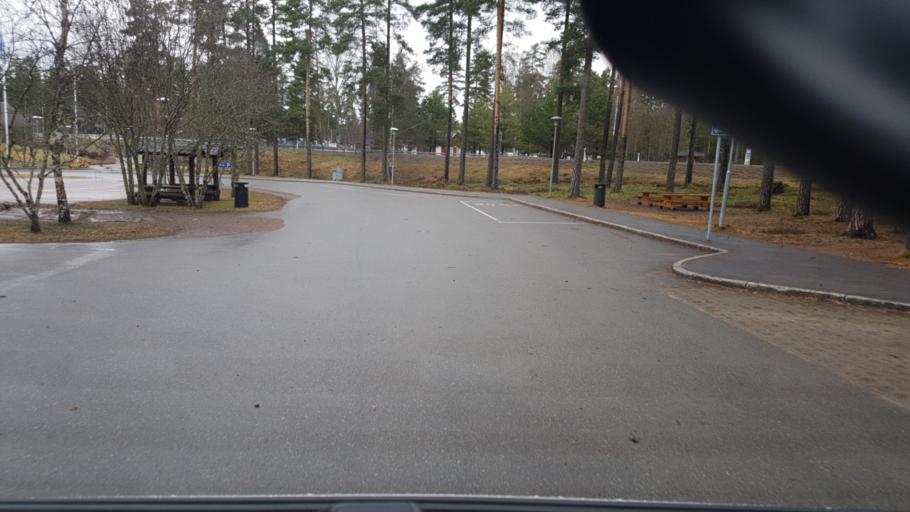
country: SE
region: Vaermland
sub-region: Eda Kommun
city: Charlottenberg
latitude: 59.9299
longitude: 12.2415
